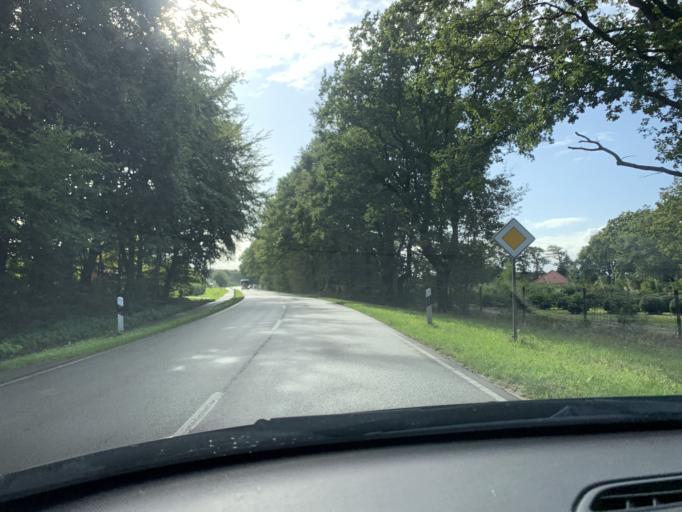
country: DE
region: Lower Saxony
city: Bad Zwischenahn
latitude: 53.1899
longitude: 7.9717
